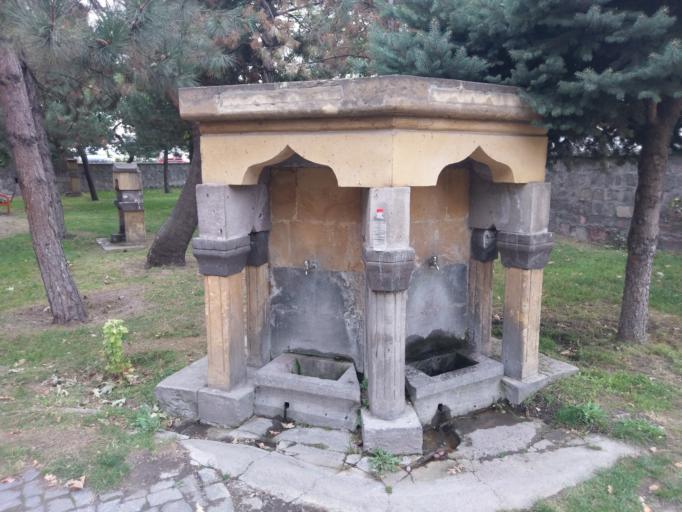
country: TR
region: Kayseri
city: Kayseri
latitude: 38.7163
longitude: 35.4897
